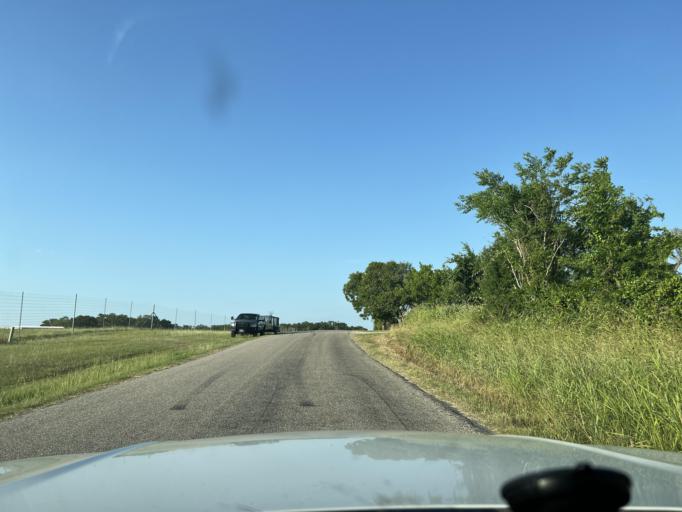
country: US
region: Texas
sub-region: Washington County
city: Brenham
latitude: 30.2093
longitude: -96.3723
